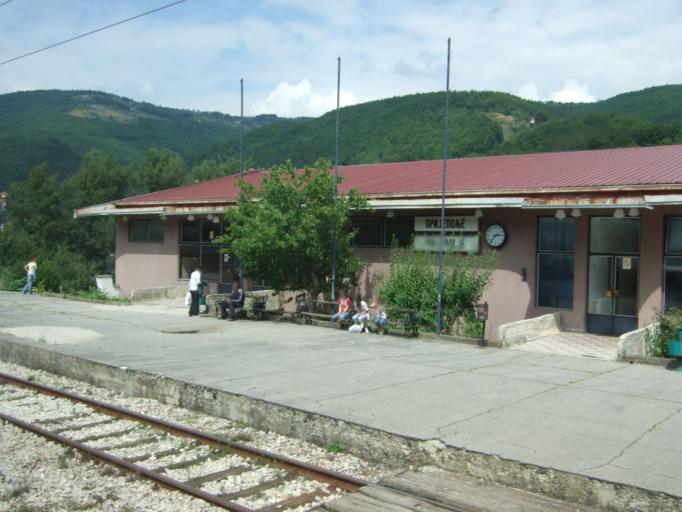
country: RS
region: Central Serbia
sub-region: Zlatiborski Okrug
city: Prijepolje
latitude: 43.3925
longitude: 19.6402
